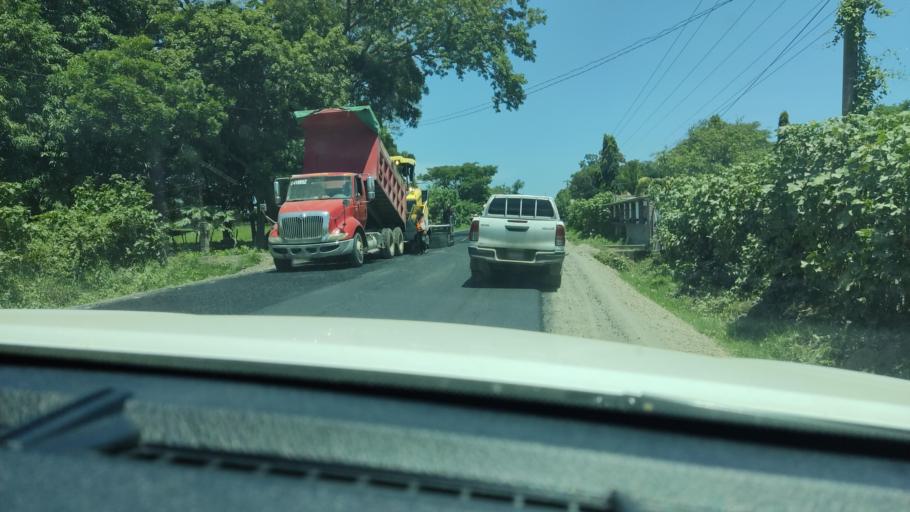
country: SV
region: Ahuachapan
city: San Francisco Menendez
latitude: 13.8413
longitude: -90.1207
